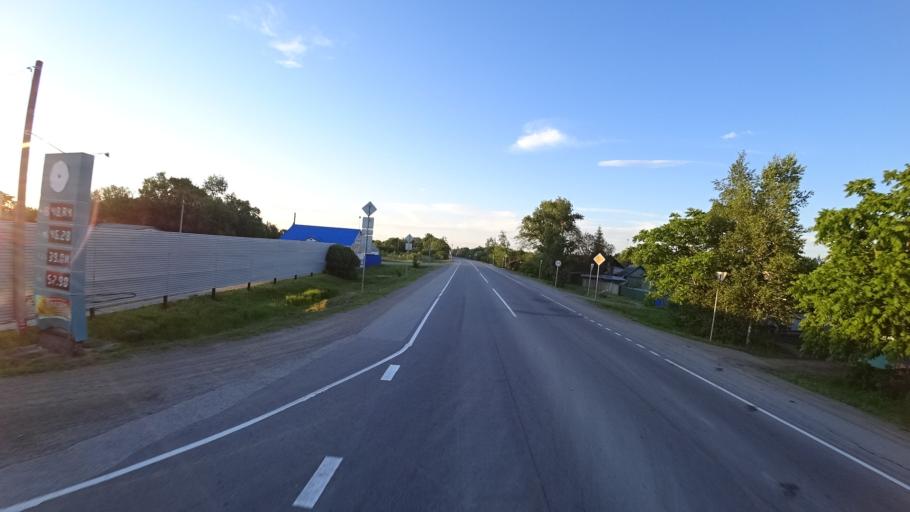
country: RU
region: Khabarovsk Krai
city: Khor
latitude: 47.8532
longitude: 134.9611
